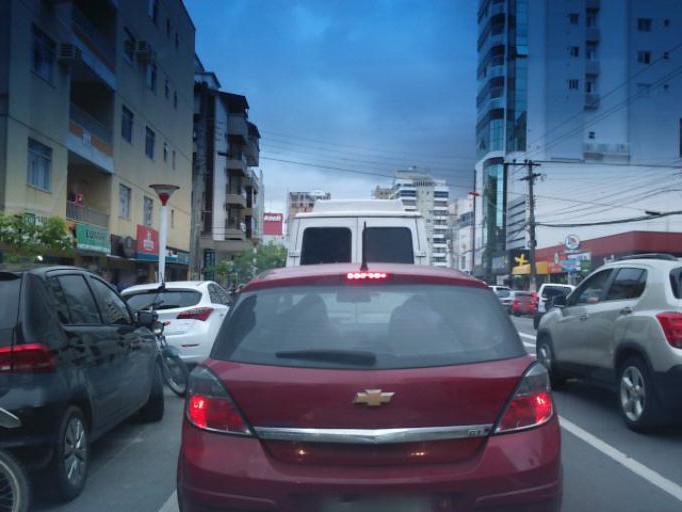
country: BR
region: Santa Catarina
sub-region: Itapema
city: Itapema
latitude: -27.1263
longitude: -48.6031
